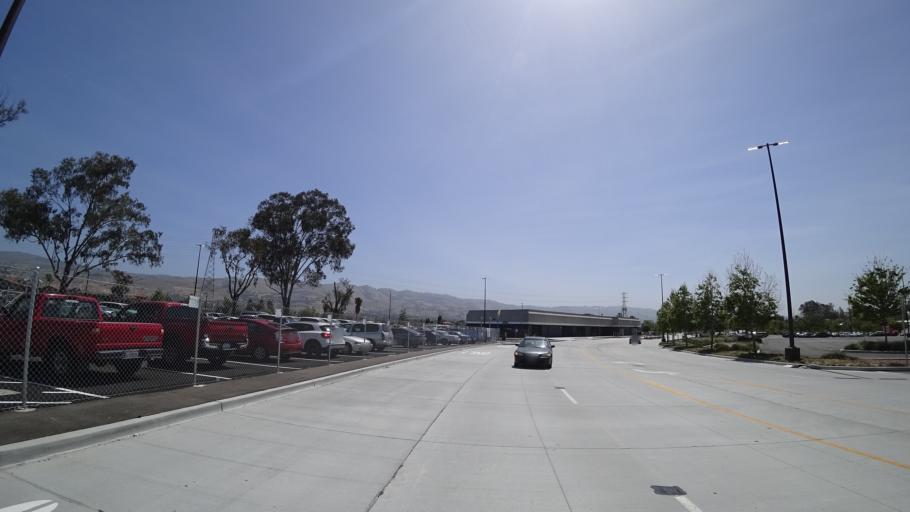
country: US
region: California
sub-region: Santa Clara County
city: Alum Rock
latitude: 37.3289
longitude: -121.8133
